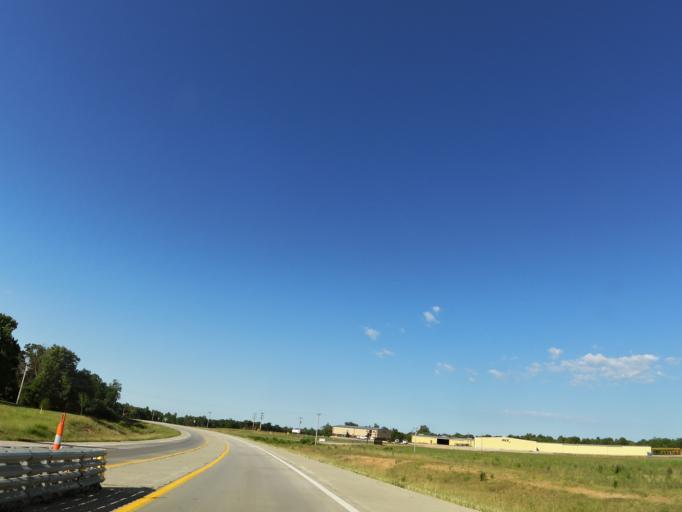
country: US
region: Missouri
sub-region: Butler County
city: Poplar Bluff
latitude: 36.6604
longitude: -90.5186
